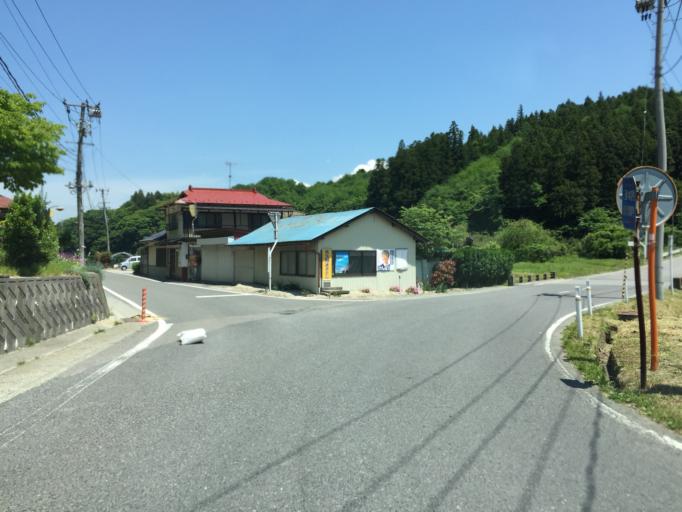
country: JP
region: Fukushima
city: Funehikimachi-funehiki
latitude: 37.4886
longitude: 140.5463
